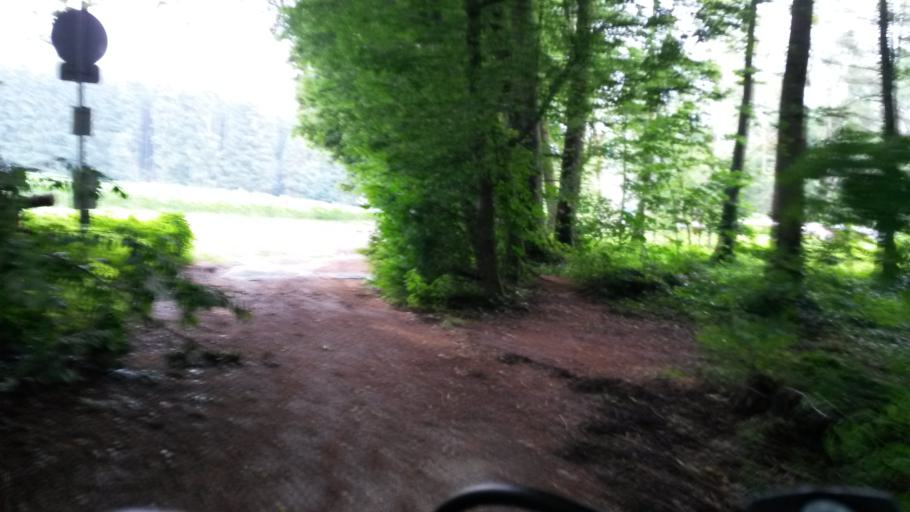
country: DE
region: Bavaria
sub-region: Upper Bavaria
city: Hoslwang
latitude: 47.9220
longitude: 12.3412
